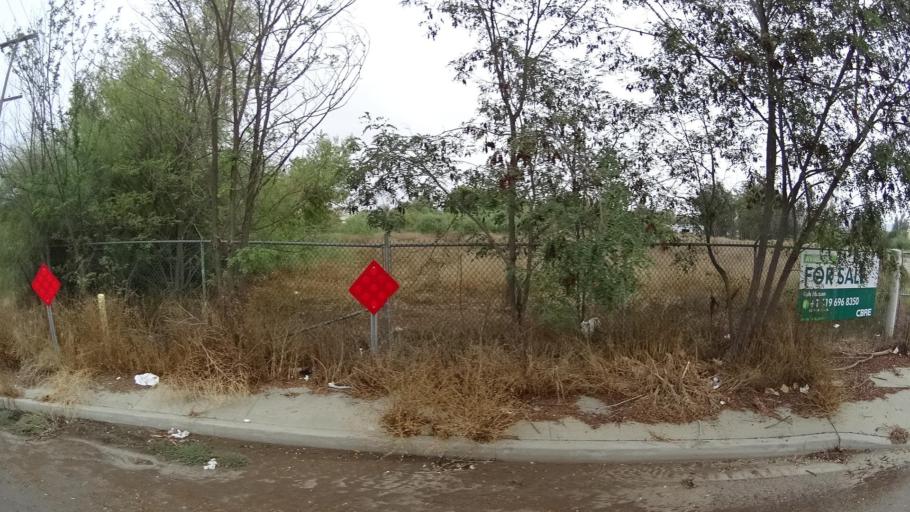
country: US
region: California
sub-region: San Diego County
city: Ramona
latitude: 33.0422
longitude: -116.8732
